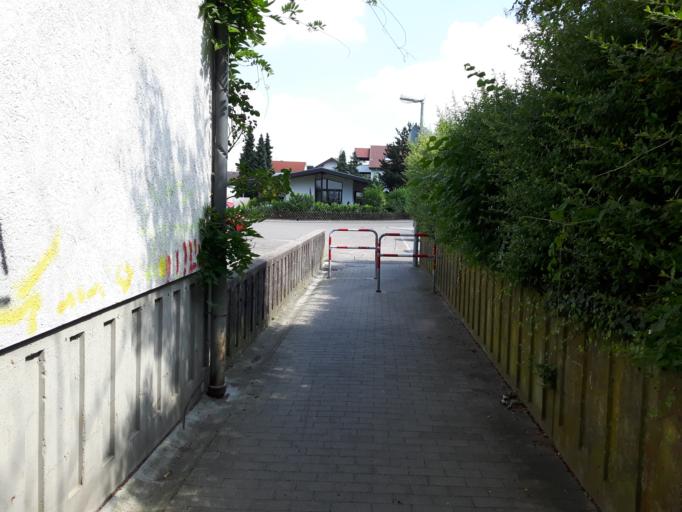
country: DE
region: Baden-Wuerttemberg
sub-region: Karlsruhe Region
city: Karlsdorf-Neuthard
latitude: 49.0972
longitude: 8.5318
